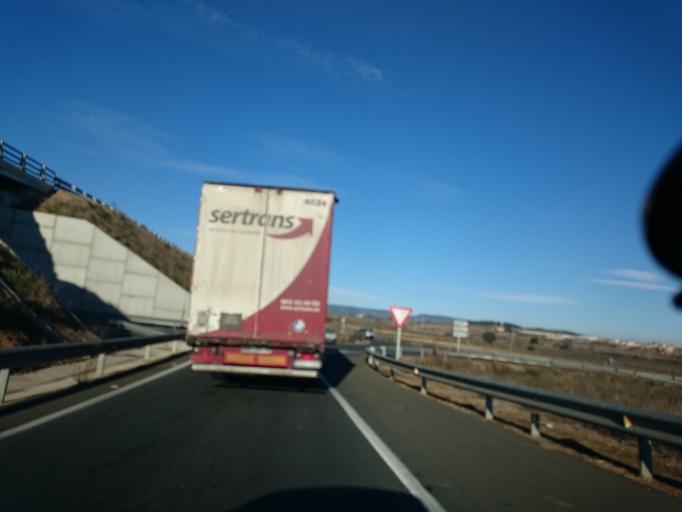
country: ES
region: Catalonia
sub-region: Provincia de Barcelona
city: La Granada
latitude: 41.3661
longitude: 1.7175
